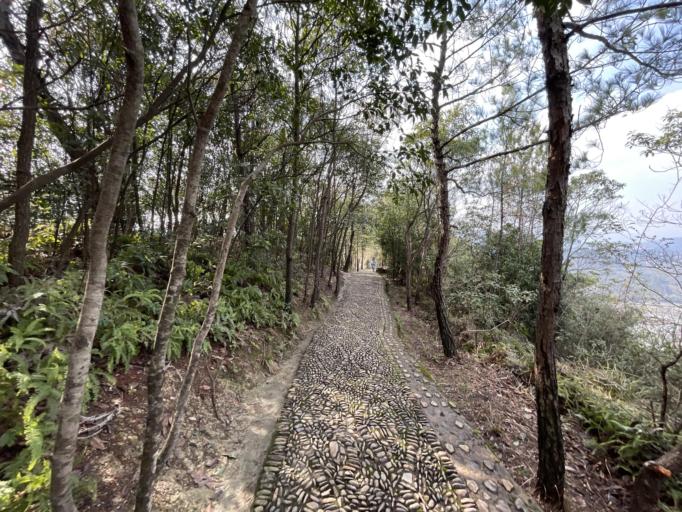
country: CN
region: Zhejiang Sheng
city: Shuhong
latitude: 28.6924
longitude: 120.1418
